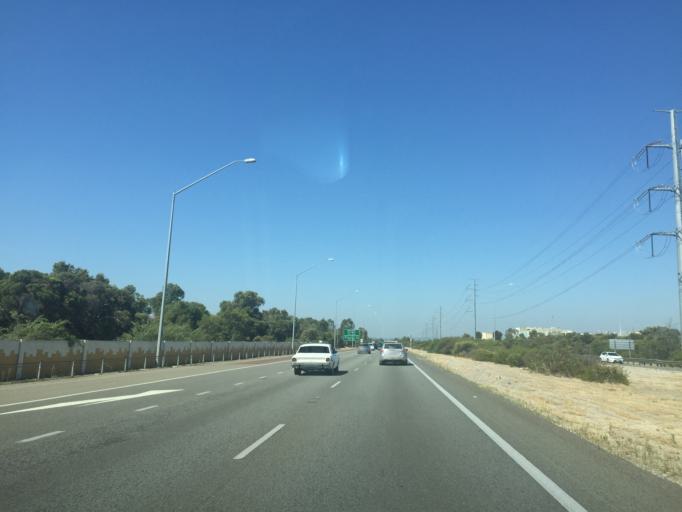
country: AU
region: Western Australia
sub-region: Canning
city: Willetton
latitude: -32.0643
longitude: 115.8956
